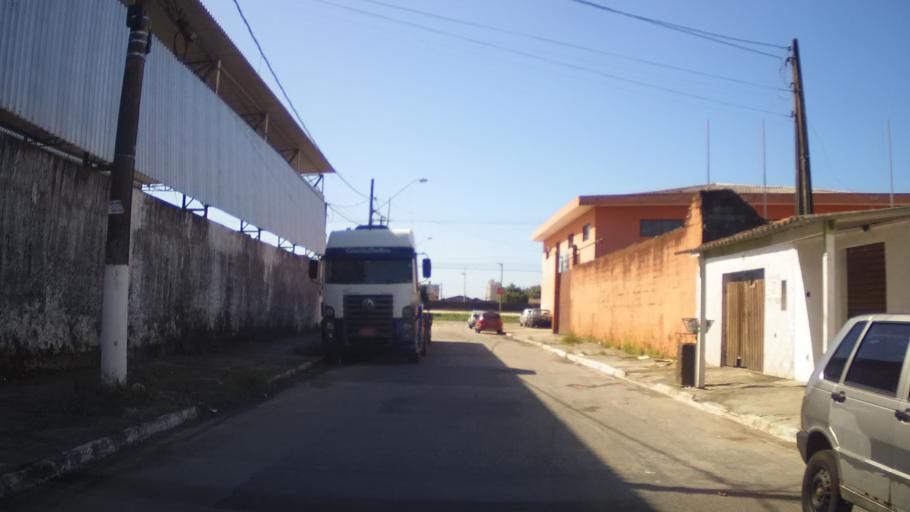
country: BR
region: Sao Paulo
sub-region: Praia Grande
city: Praia Grande
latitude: -24.0343
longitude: -46.5138
